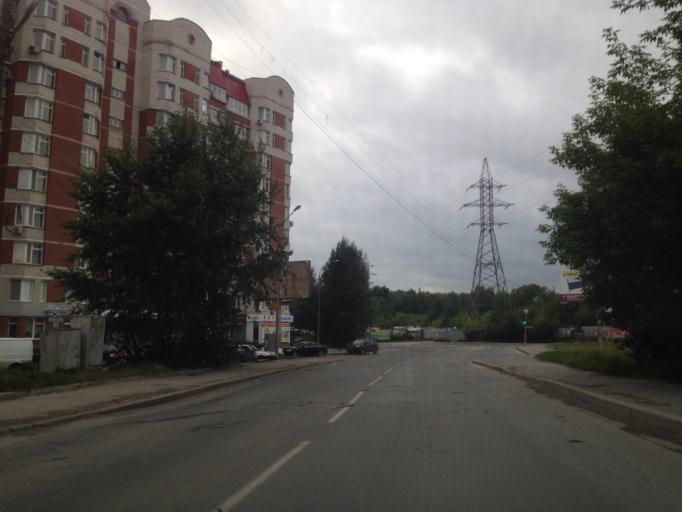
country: RU
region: Sverdlovsk
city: Yekaterinburg
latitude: 56.8420
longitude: 60.6914
